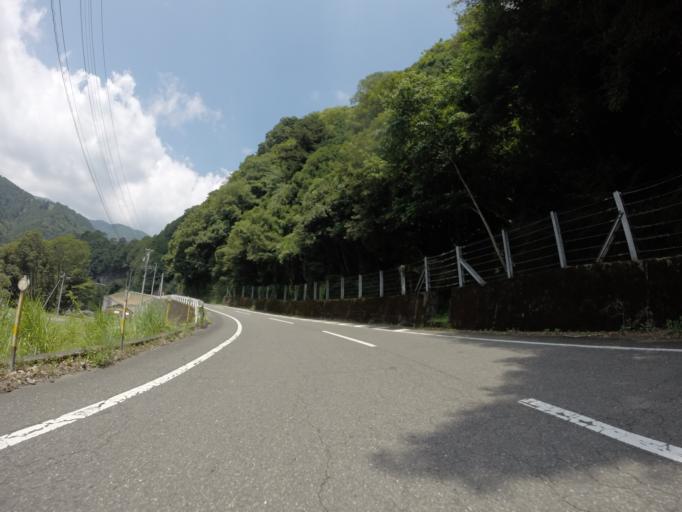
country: JP
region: Shizuoka
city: Shizuoka-shi
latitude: 35.2498
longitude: 138.3425
